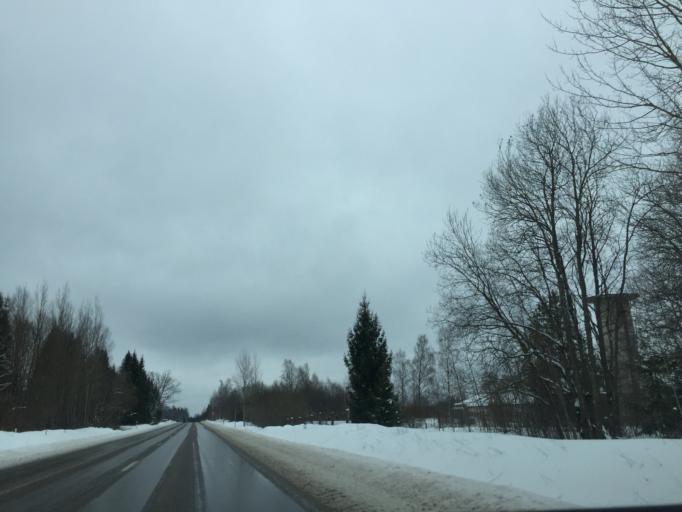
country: LV
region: Ligatne
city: Ligatne
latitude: 57.1754
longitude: 25.0409
